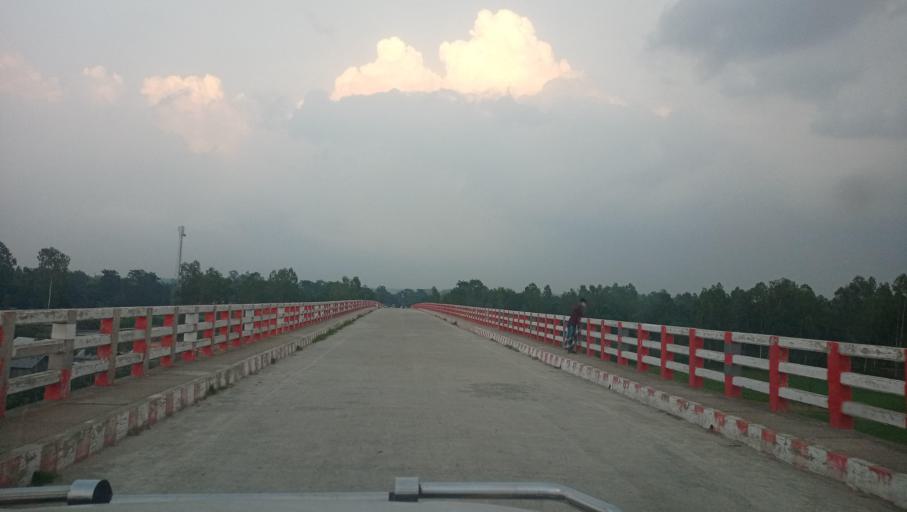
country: BD
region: Dhaka
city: Sherpur
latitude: 25.1768
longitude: 89.7921
